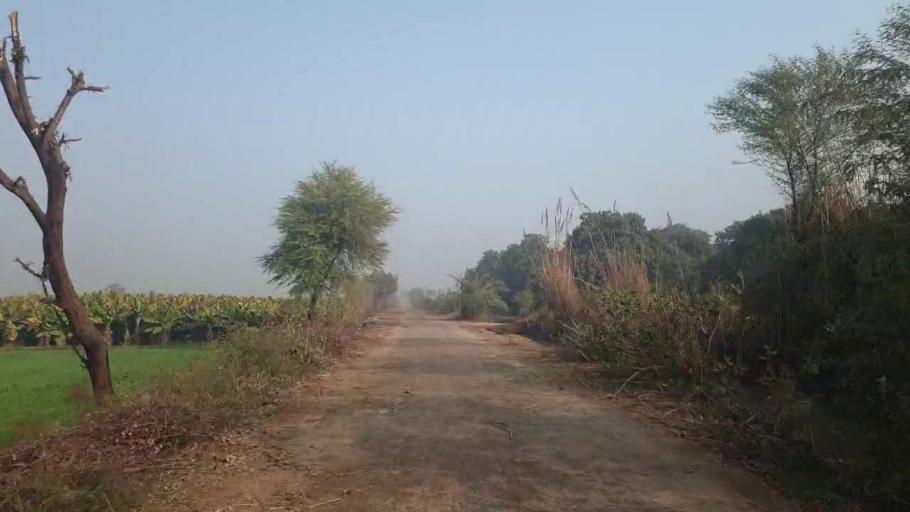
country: PK
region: Sindh
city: Tando Adam
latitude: 25.8139
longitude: 68.6323
